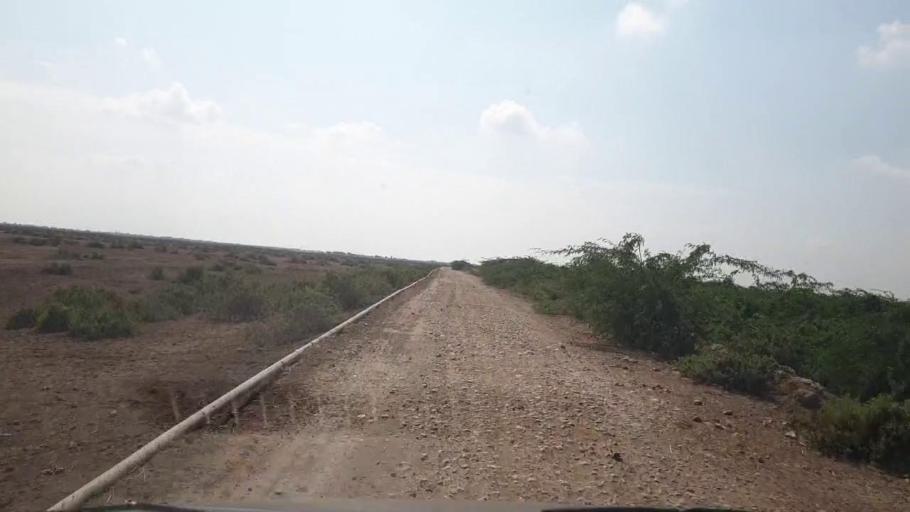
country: PK
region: Sindh
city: Badin
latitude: 24.5056
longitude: 68.6081
